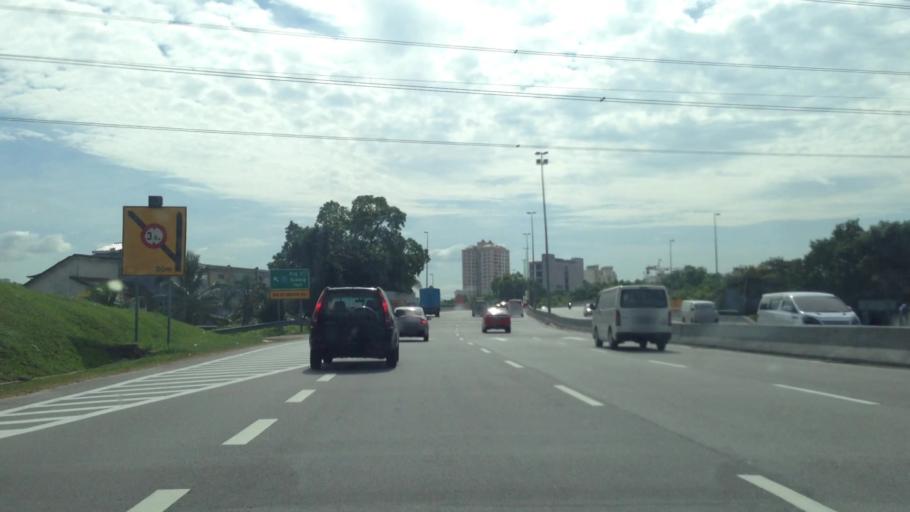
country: MY
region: Selangor
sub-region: Petaling
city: Petaling Jaya
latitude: 3.0762
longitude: 101.6198
